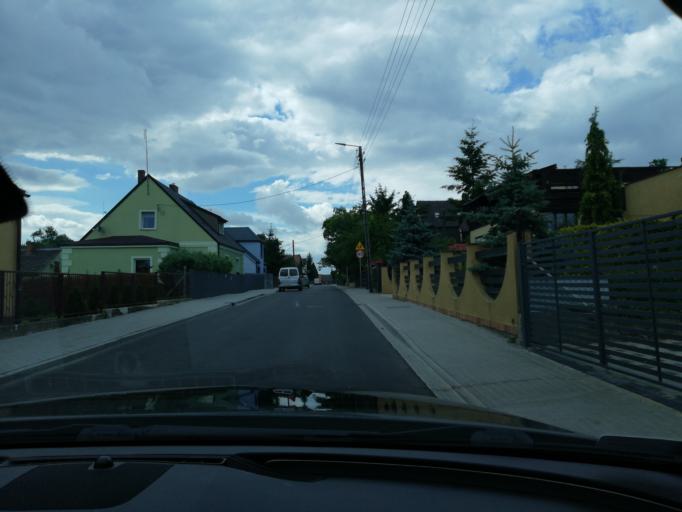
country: PL
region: Greater Poland Voivodeship
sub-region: Powiat poznanski
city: Murowana Goslina
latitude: 52.5767
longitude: 17.0153
